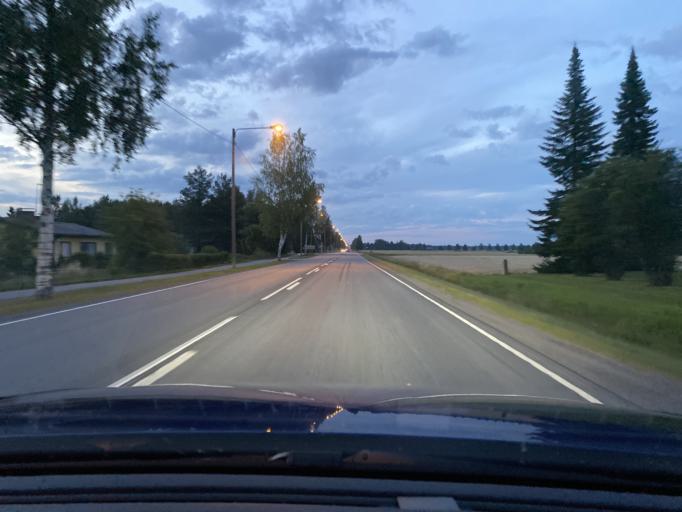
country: FI
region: Southern Ostrobothnia
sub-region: Suupohja
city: Kauhajoki
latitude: 62.4313
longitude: 22.2045
